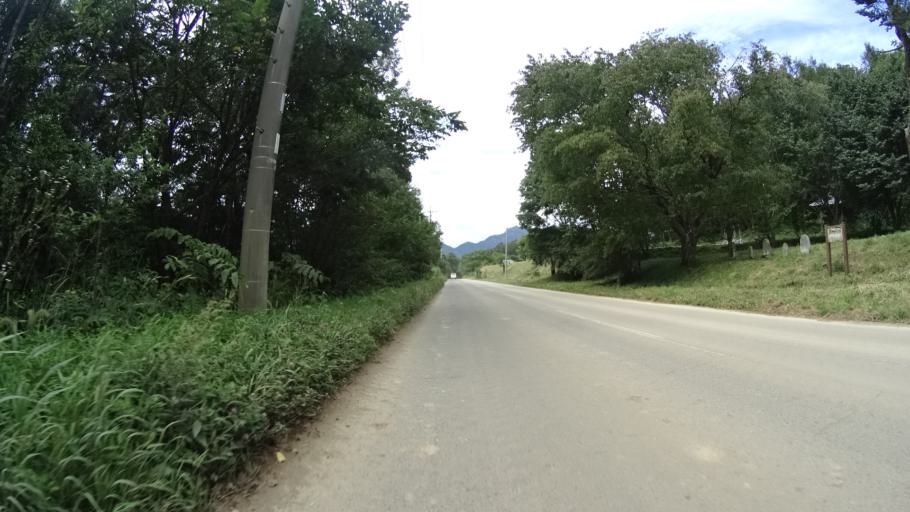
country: JP
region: Yamanashi
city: Nirasaki
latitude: 35.9446
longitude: 138.5482
